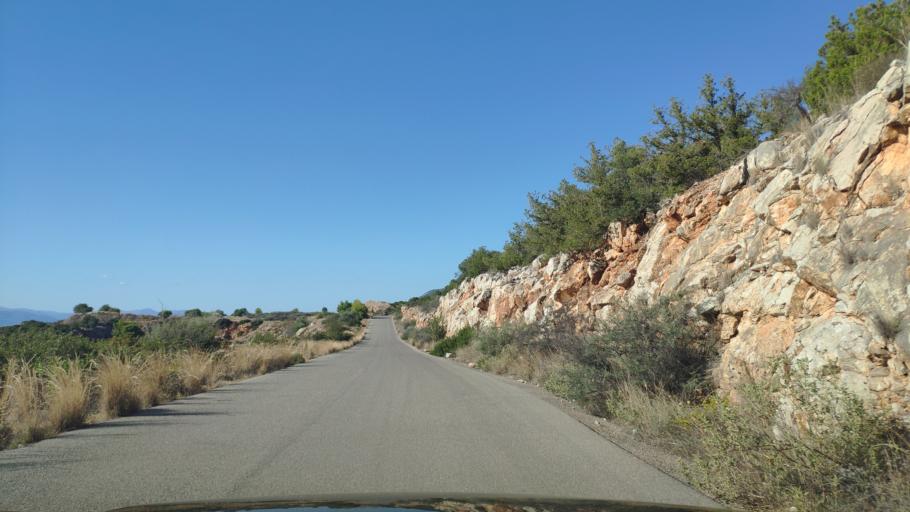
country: GR
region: Attica
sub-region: Nomos Piraios
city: Galatas
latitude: 37.5650
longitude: 23.3624
